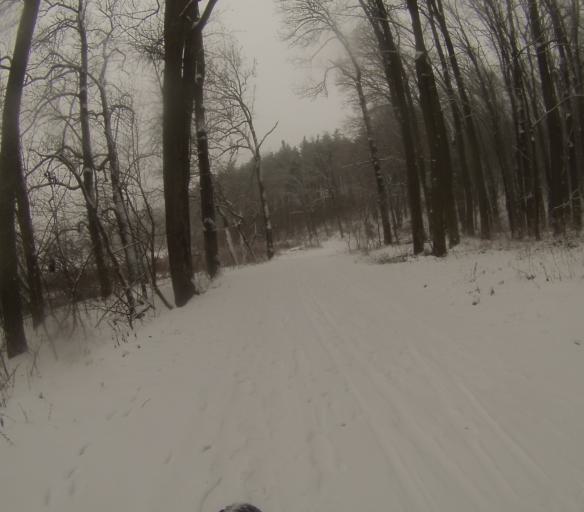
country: CZ
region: South Moravian
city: Strelice
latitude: 49.1398
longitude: 16.4886
